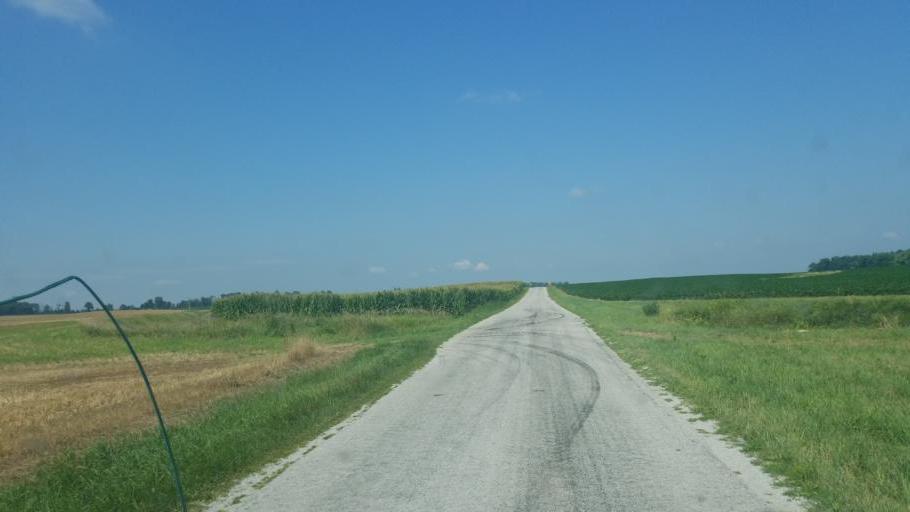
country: US
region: Ohio
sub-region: Hardin County
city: Kenton
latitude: 40.6750
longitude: -83.6299
